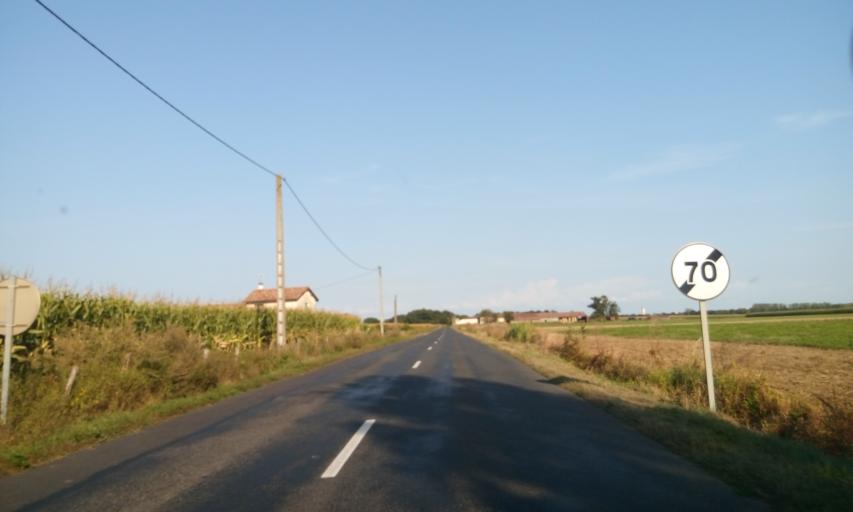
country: FR
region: Rhone-Alpes
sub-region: Departement de l'Ain
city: Amberieux-en-Dombes
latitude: 46.0012
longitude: 4.8701
